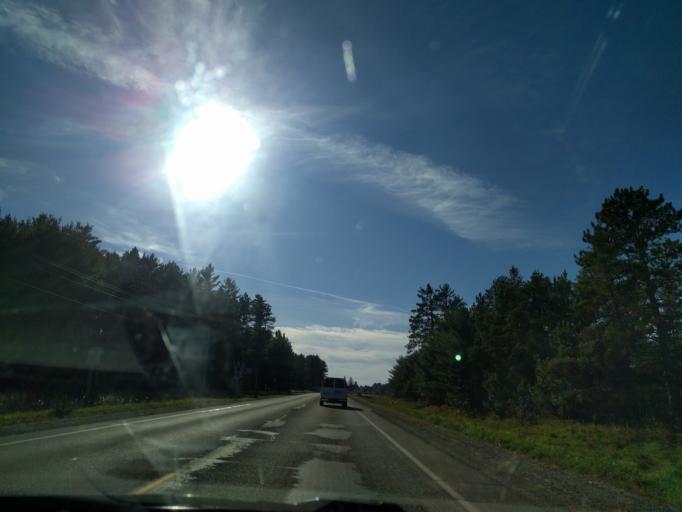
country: US
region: Wisconsin
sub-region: Marinette County
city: Niagara
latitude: 45.6387
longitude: -87.9826
